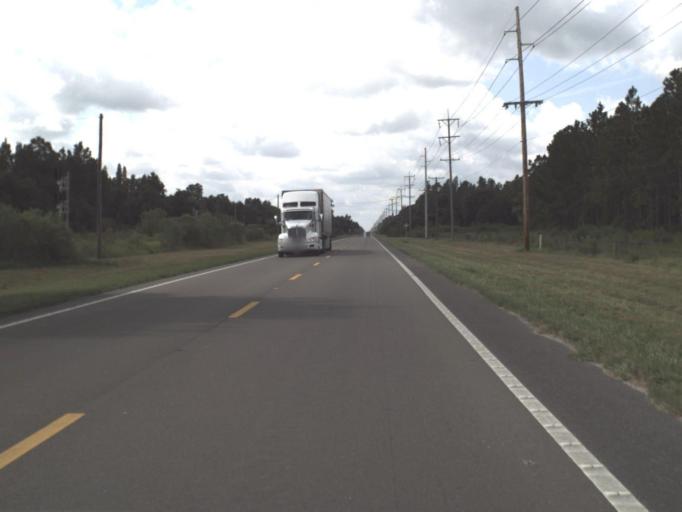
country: US
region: Florida
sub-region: Pasco County
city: Crystal Springs
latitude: 28.1588
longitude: -82.1536
